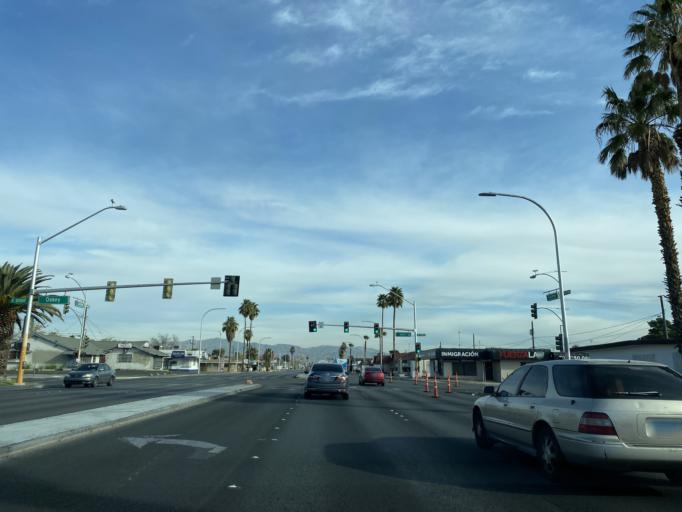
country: US
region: Nevada
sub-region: Clark County
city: Winchester
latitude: 36.1512
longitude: -115.1188
